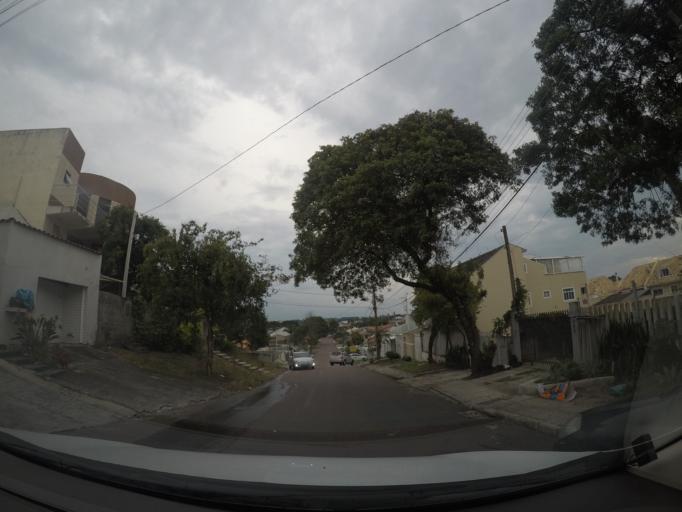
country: BR
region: Parana
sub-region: Curitiba
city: Curitiba
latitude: -25.4707
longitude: -49.2426
